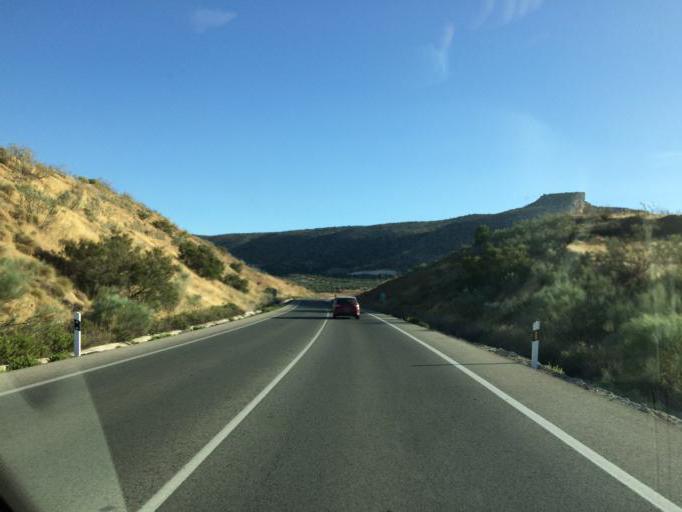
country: ES
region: Andalusia
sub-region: Provincia de Malaga
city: Teba
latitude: 36.9562
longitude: -4.8585
